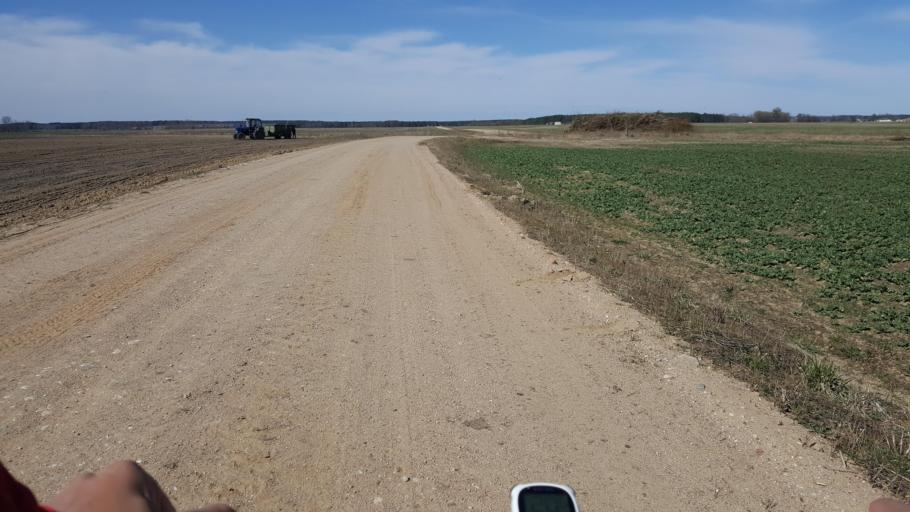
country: BY
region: Brest
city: Kamyanyets
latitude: 52.3018
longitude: 23.9072
